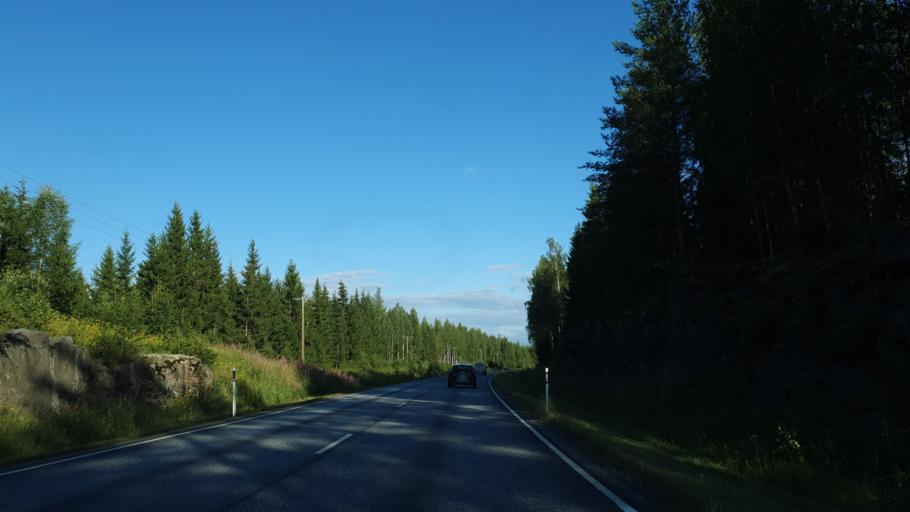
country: FI
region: North Karelia
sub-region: Joensuu
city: Outokumpu
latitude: 62.5309
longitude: 28.9811
